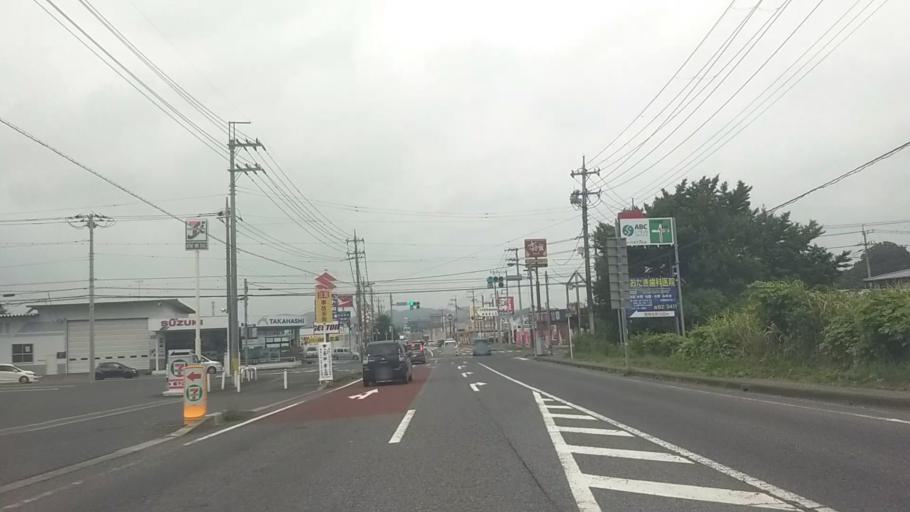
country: JP
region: Chiba
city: Ohara
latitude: 35.2854
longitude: 140.2525
